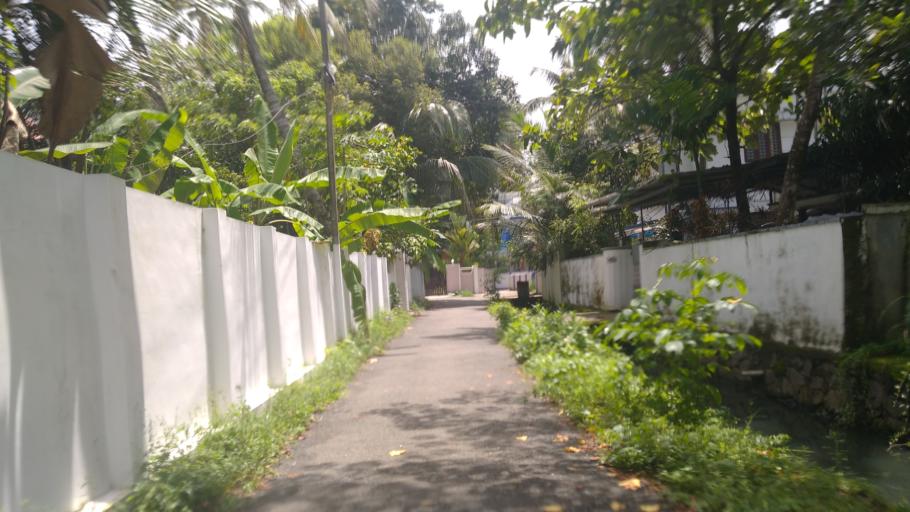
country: IN
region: Kerala
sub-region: Ernakulam
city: Elur
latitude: 10.0614
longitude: 76.2155
